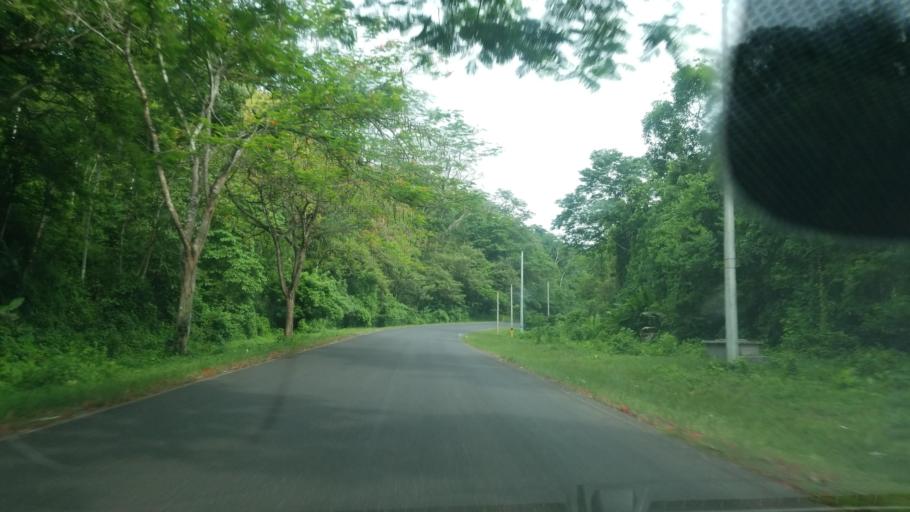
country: HN
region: Santa Barbara
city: Petoa
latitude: 15.2355
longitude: -88.2678
